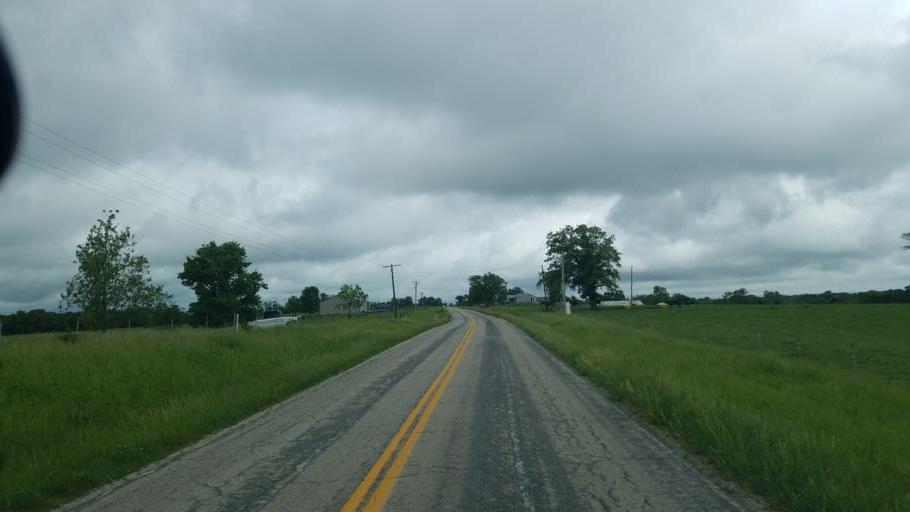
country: US
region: Missouri
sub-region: Mercer County
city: Princeton
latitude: 40.3359
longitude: -93.6836
